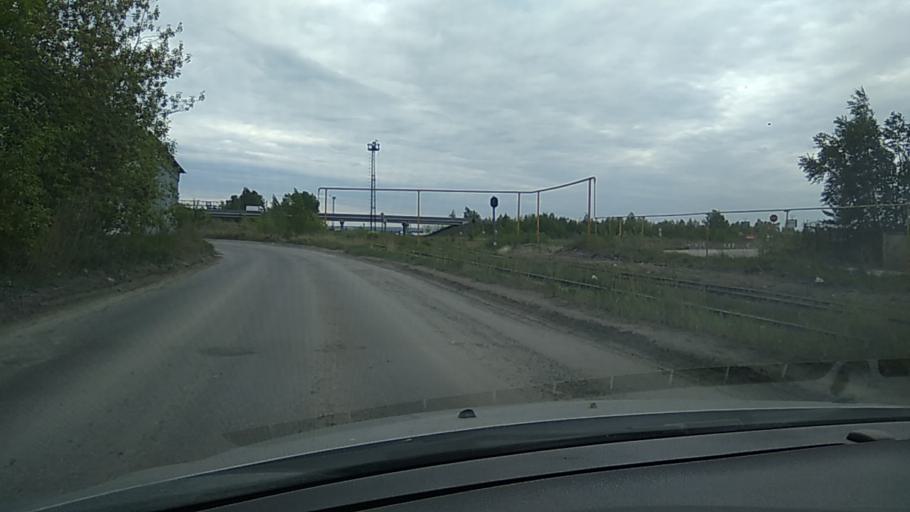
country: RU
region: Sverdlovsk
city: Istok
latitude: 56.7541
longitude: 60.7524
